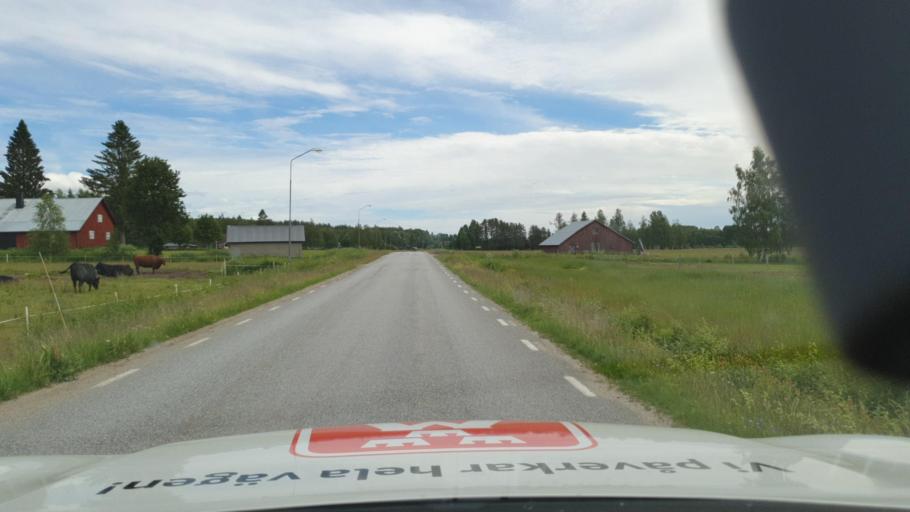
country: SE
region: Vaesterbotten
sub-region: Skelleftea Kommun
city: Burea
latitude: 64.5050
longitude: 21.0096
